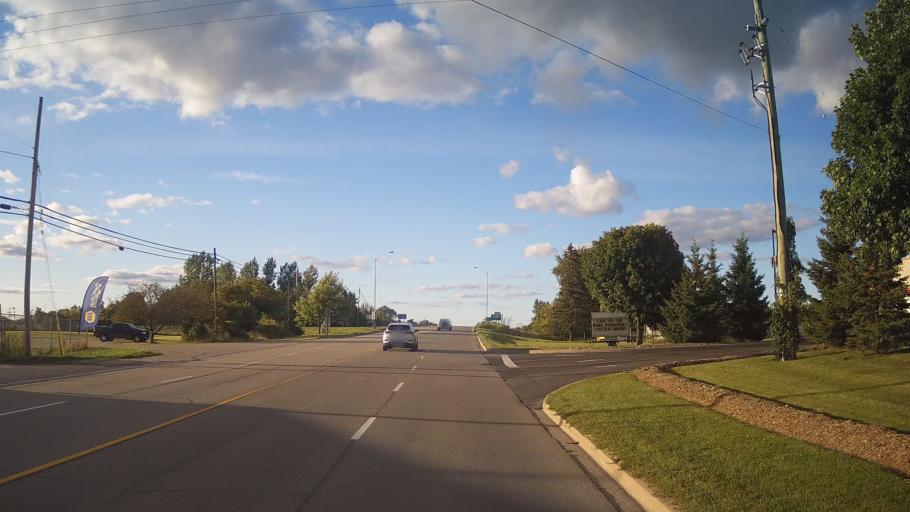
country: CA
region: Ontario
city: Gananoque
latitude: 44.3414
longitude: -76.1702
